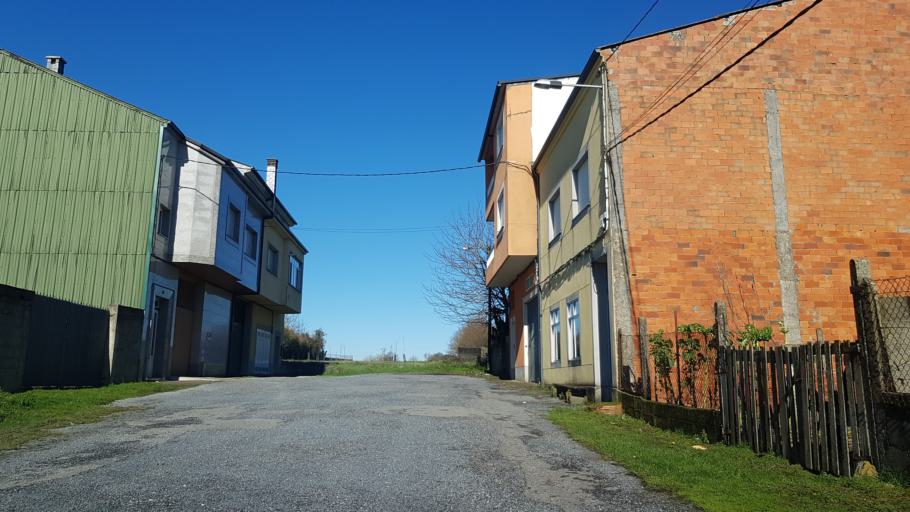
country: ES
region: Galicia
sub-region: Provincia de Lugo
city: Lugo
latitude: 43.0185
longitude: -7.5760
